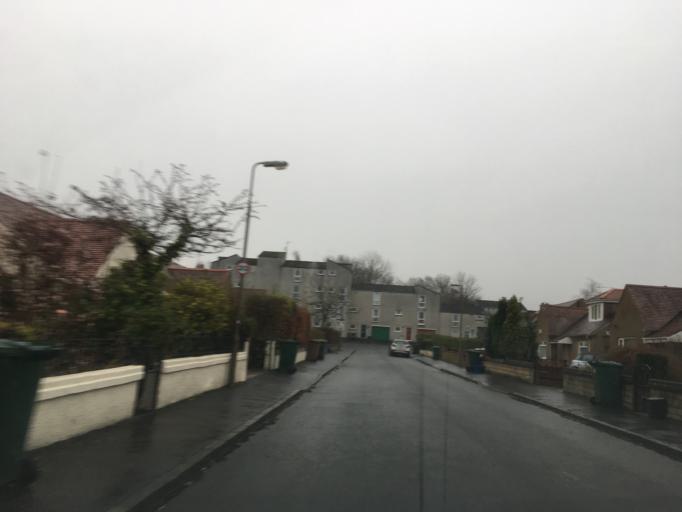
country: GB
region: Scotland
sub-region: Edinburgh
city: Currie
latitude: 55.9584
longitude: -3.3019
